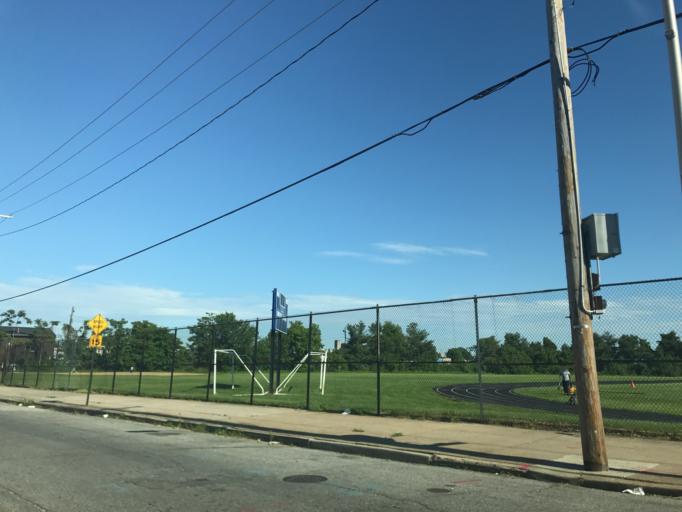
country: US
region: Maryland
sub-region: City of Baltimore
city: Baltimore
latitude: 39.3052
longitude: -76.6510
